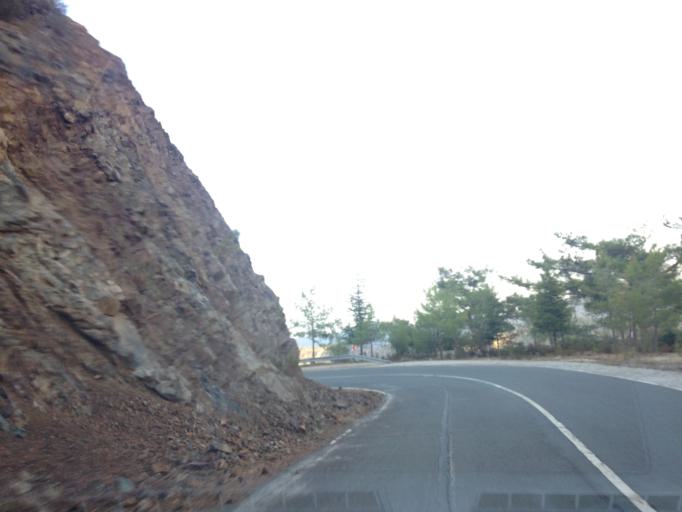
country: CY
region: Lefkosia
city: Lefka
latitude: 34.9994
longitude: 32.7355
